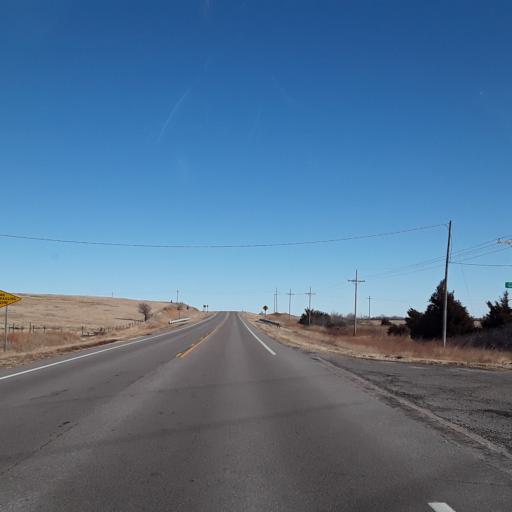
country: US
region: Kansas
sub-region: Pawnee County
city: Larned
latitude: 38.0869
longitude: -99.2268
